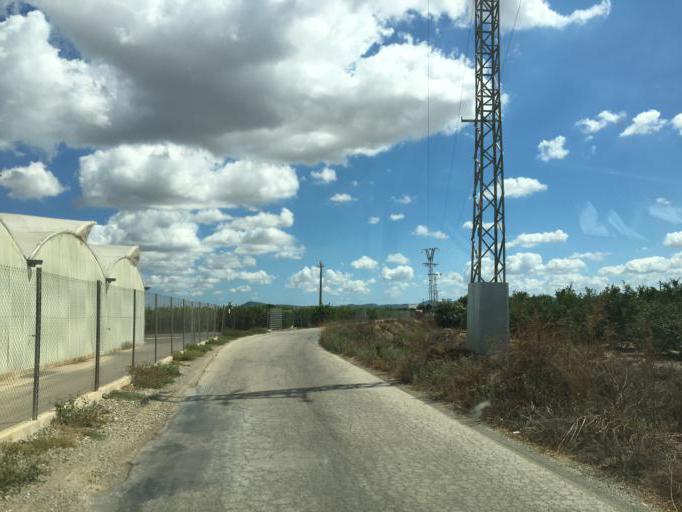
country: ES
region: Murcia
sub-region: Murcia
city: Santomera
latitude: 38.0494
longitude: -1.0509
